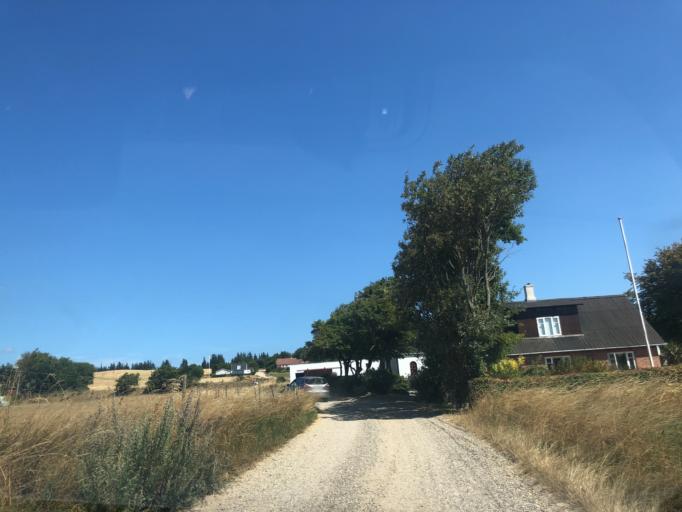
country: DK
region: North Denmark
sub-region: Morso Kommune
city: Nykobing Mors
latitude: 56.8255
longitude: 8.9949
